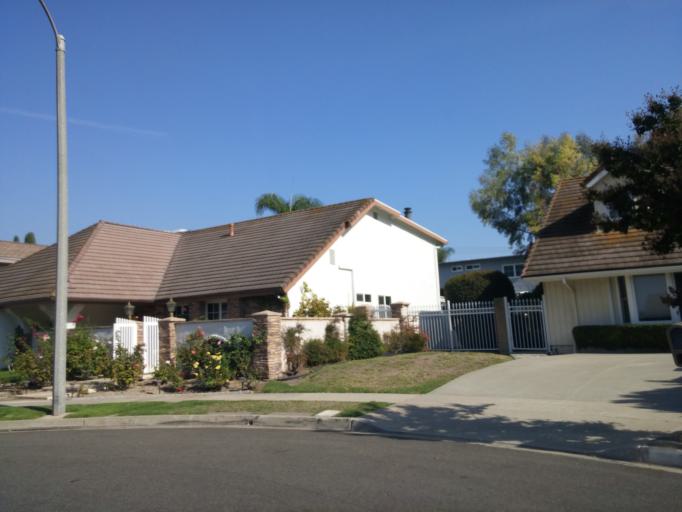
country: US
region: California
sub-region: Orange County
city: Irvine
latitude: 33.6822
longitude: -117.7781
